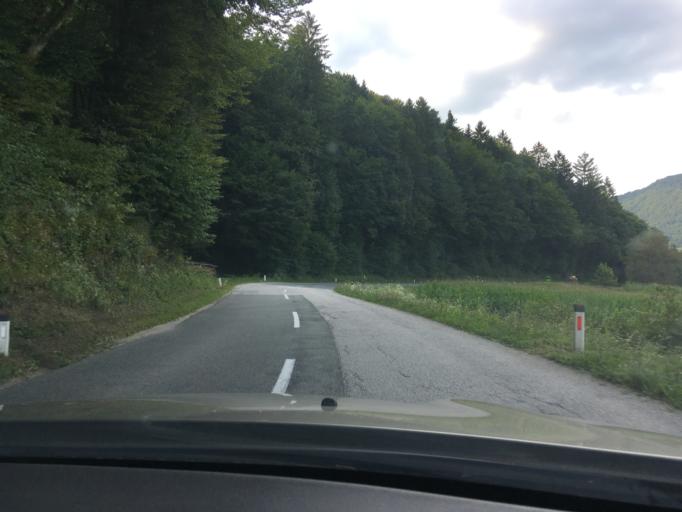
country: SI
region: Dolenjske Toplice
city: Dolenjske Toplice
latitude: 45.7708
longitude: 15.0235
